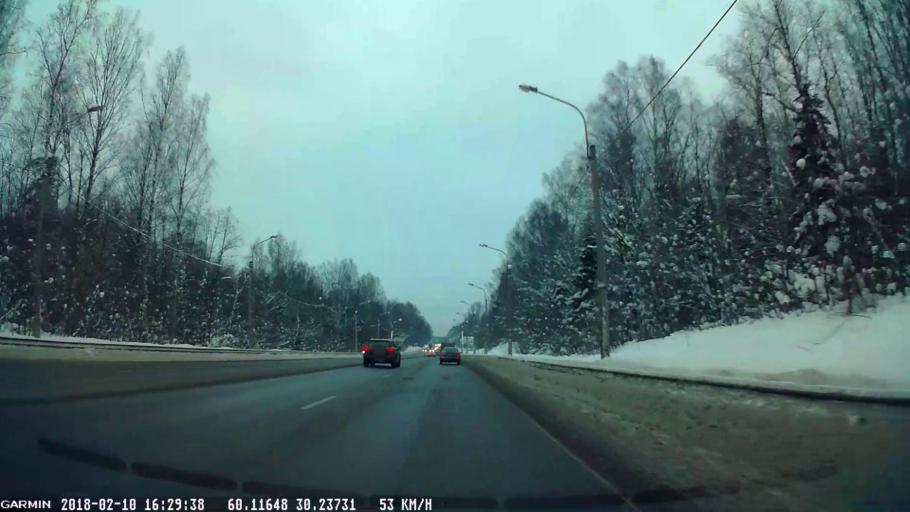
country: RU
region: St.-Petersburg
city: Levashovo
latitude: 60.1173
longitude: 30.2366
